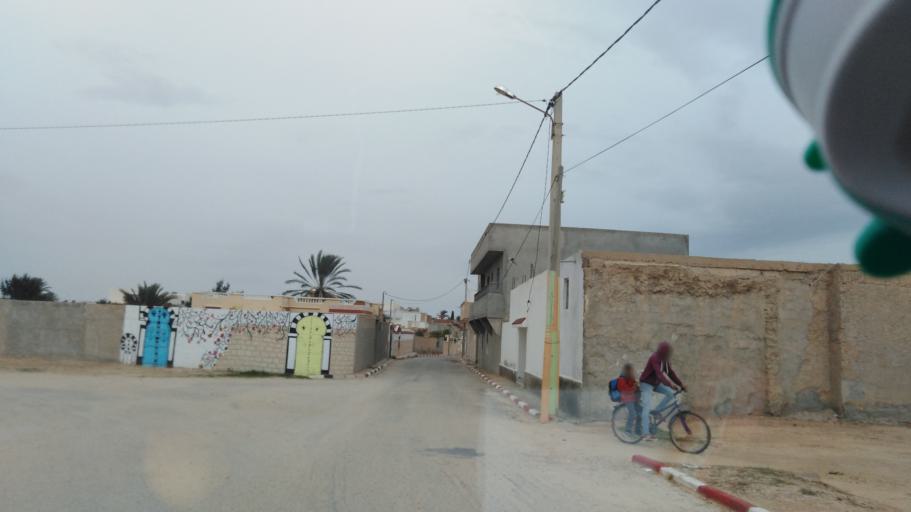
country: TN
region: Qabis
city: Gabes
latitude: 33.9568
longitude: 10.0027
